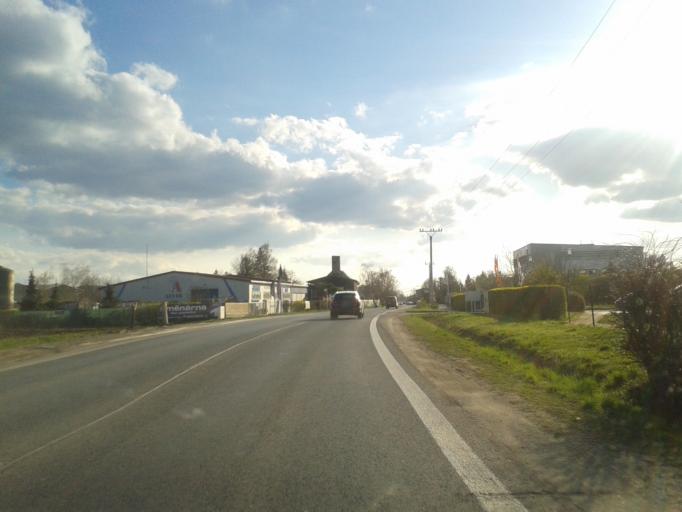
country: CZ
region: Central Bohemia
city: Rudna
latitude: 50.0480
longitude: 14.2654
